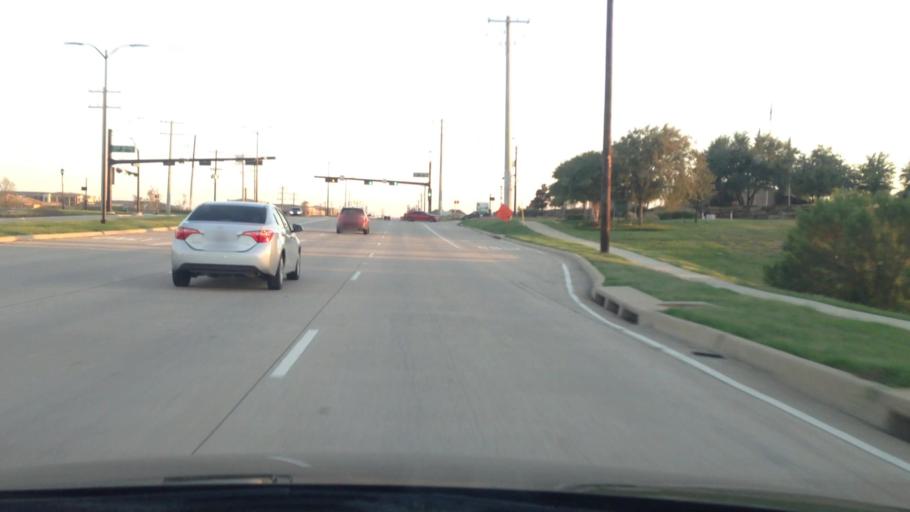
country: US
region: Texas
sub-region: Denton County
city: The Colony
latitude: 33.1374
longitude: -96.8907
